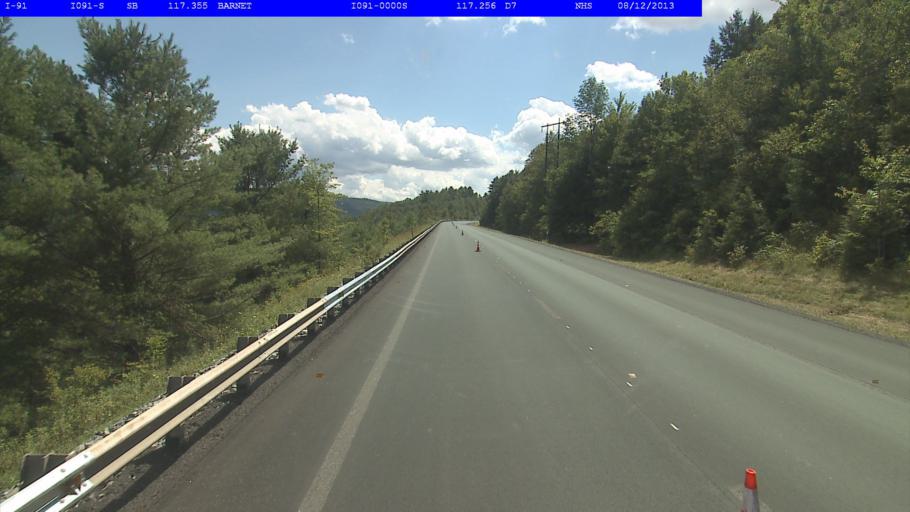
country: US
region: New Hampshire
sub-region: Grafton County
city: Woodsville
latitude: 44.2574
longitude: -72.0648
